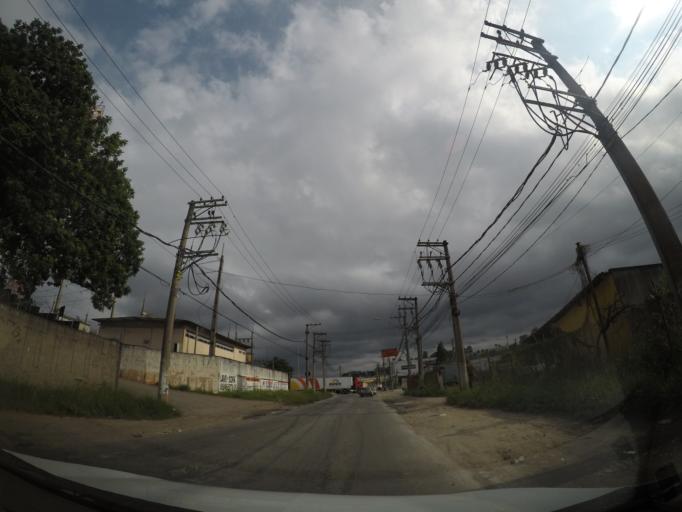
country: BR
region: Sao Paulo
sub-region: Itaquaquecetuba
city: Itaquaquecetuba
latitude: -23.4231
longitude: -46.4078
